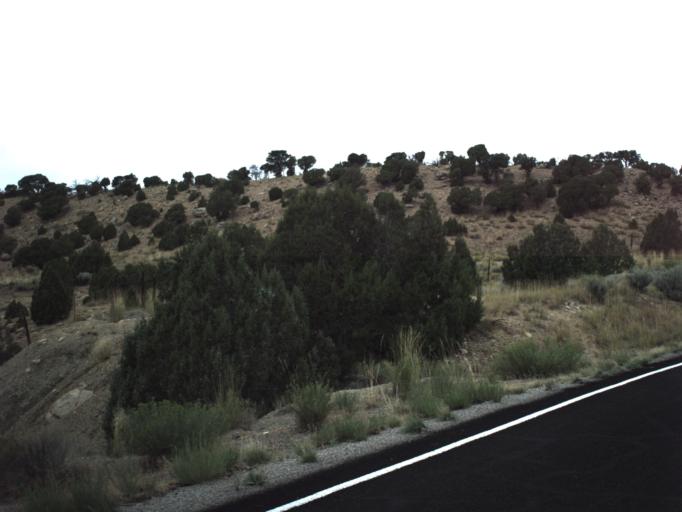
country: US
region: Utah
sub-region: Carbon County
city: East Carbon City
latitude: 39.4849
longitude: -110.4031
